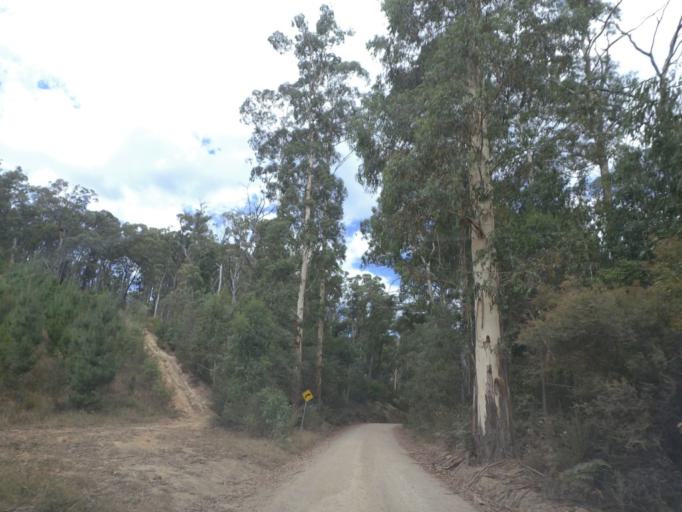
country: AU
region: Victoria
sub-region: Murrindindi
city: Alexandra
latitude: -37.3782
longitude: 145.7612
